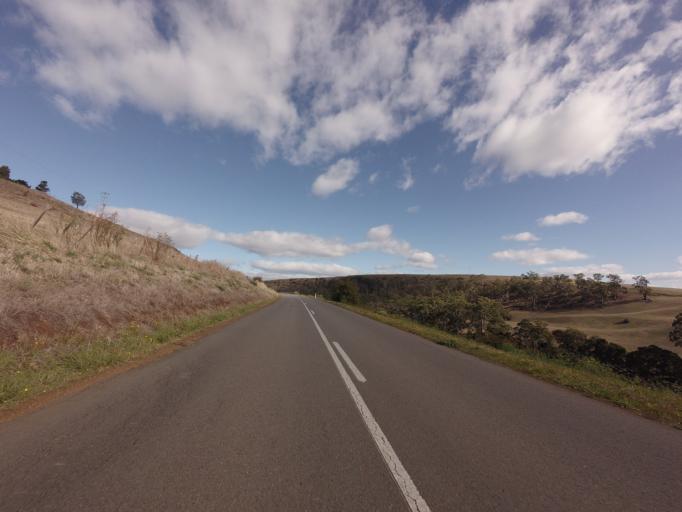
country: AU
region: Tasmania
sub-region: Derwent Valley
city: New Norfolk
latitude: -42.6977
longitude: 146.9256
